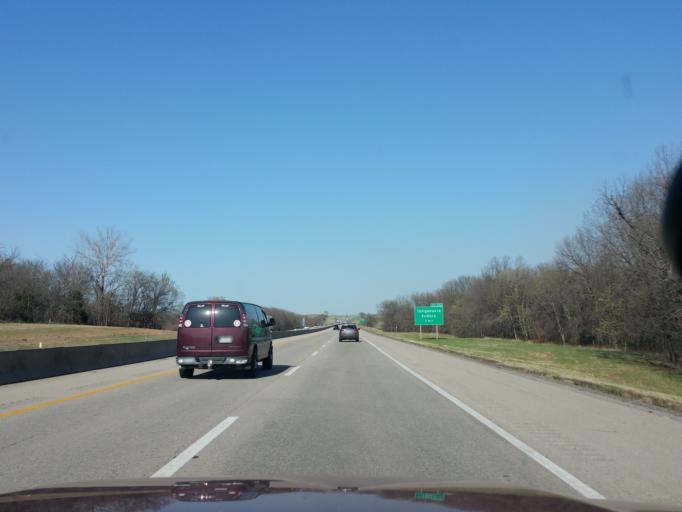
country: US
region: Kansas
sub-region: Leavenworth County
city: Tonganoxie
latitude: 39.0309
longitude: -95.1165
